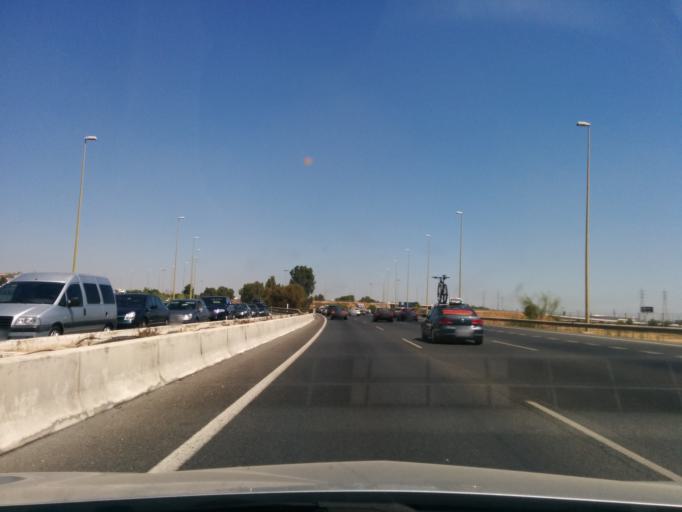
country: ES
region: Andalusia
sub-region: Provincia de Sevilla
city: Camas
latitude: 37.3834
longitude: -6.0257
